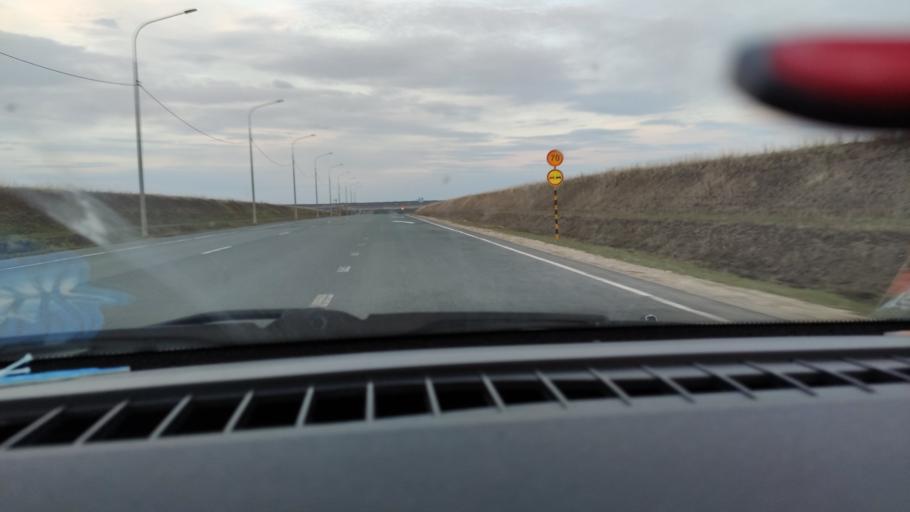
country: RU
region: Saratov
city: Yelshanka
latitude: 51.8310
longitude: 46.4479
